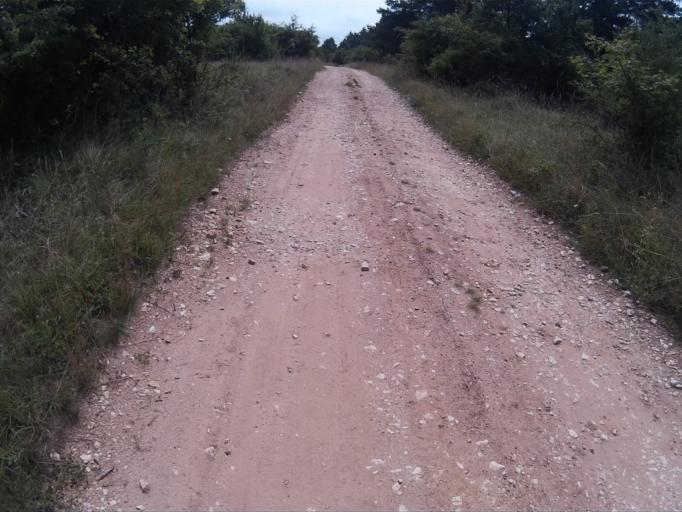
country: HU
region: Veszprem
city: Papa
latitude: 47.2952
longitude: 17.6240
